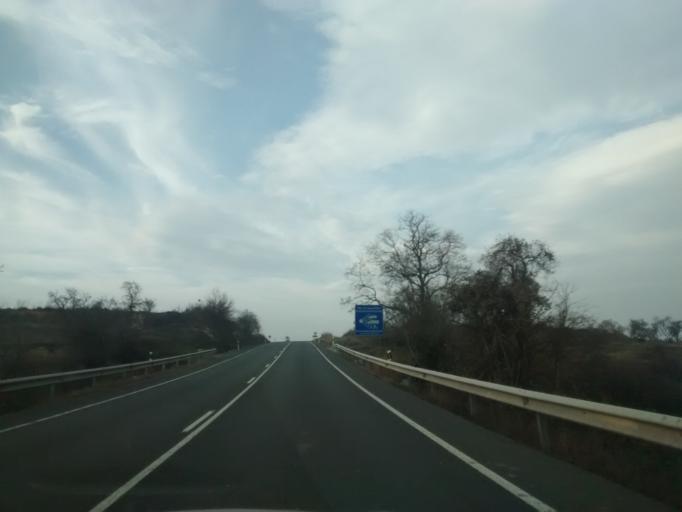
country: ES
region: La Rioja
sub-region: Provincia de La Rioja
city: Briones
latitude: 42.5307
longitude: -2.7624
